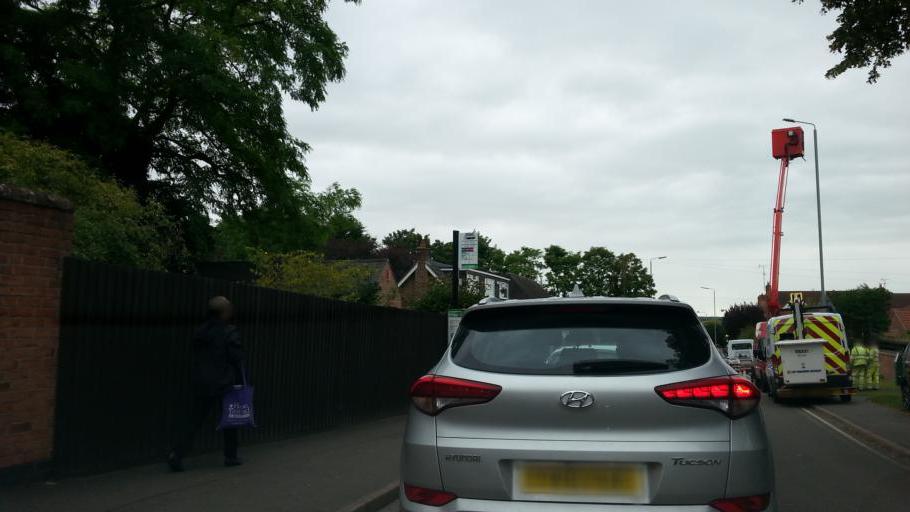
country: GB
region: England
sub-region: Nottinghamshire
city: Southwell
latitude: 53.0790
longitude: -0.9572
